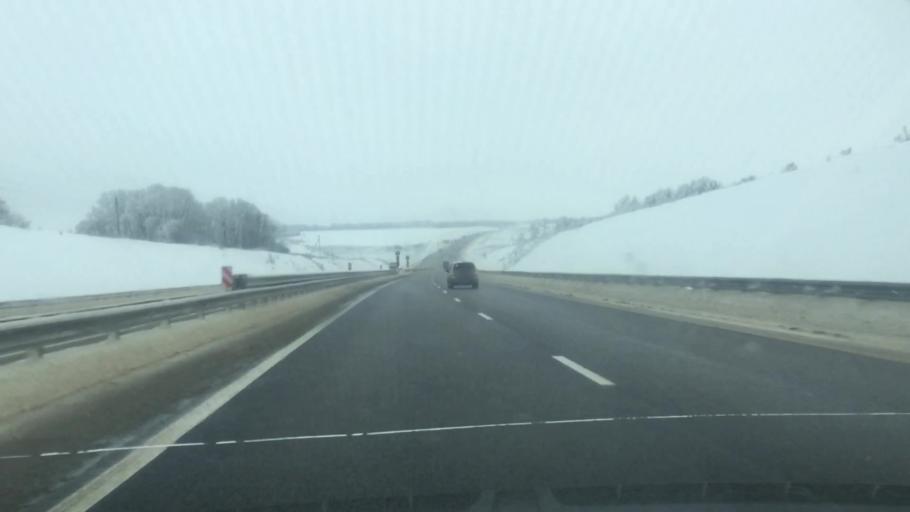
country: RU
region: Lipetsk
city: Stanovoye
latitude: 52.8716
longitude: 38.2799
